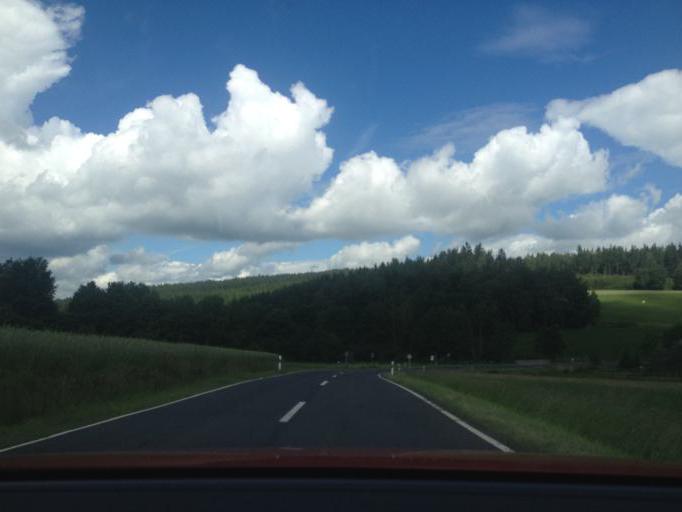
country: DE
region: Bavaria
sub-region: Upper Franconia
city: Arzberg
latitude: 50.0321
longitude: 12.2001
